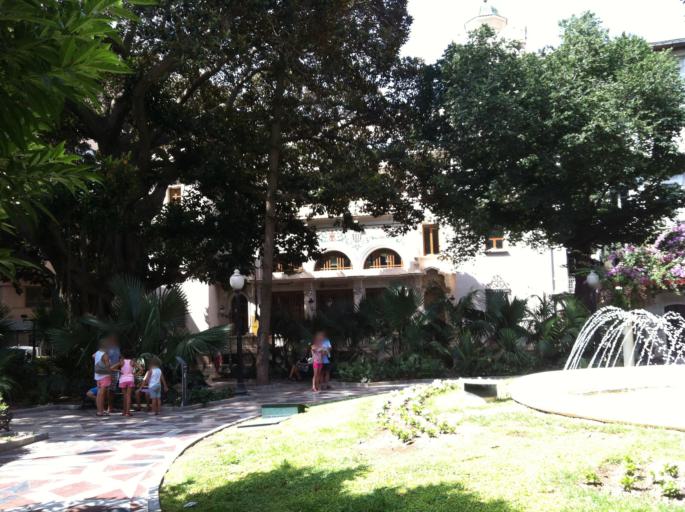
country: ES
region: Valencia
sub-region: Provincia de Alicante
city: Alicante
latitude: 38.3432
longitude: -0.4848
